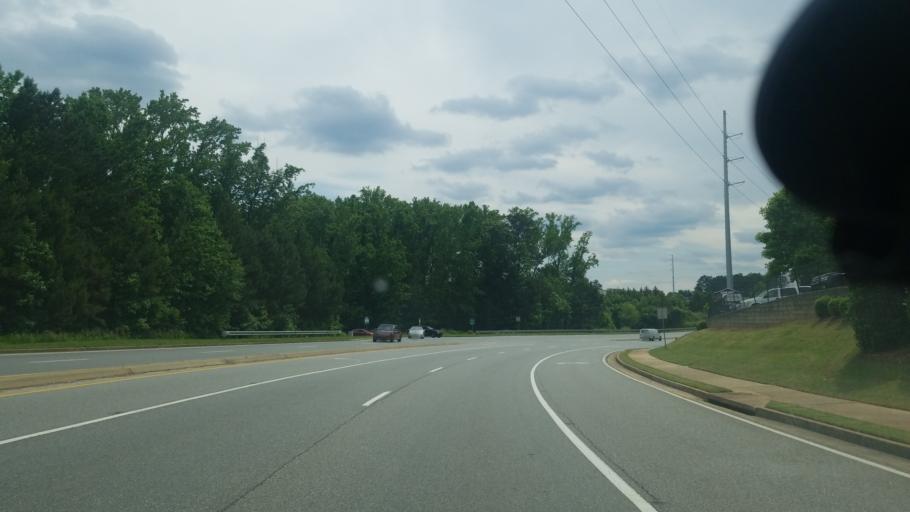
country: US
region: Georgia
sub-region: Forsyth County
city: Cumming
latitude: 34.1525
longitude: -84.1694
